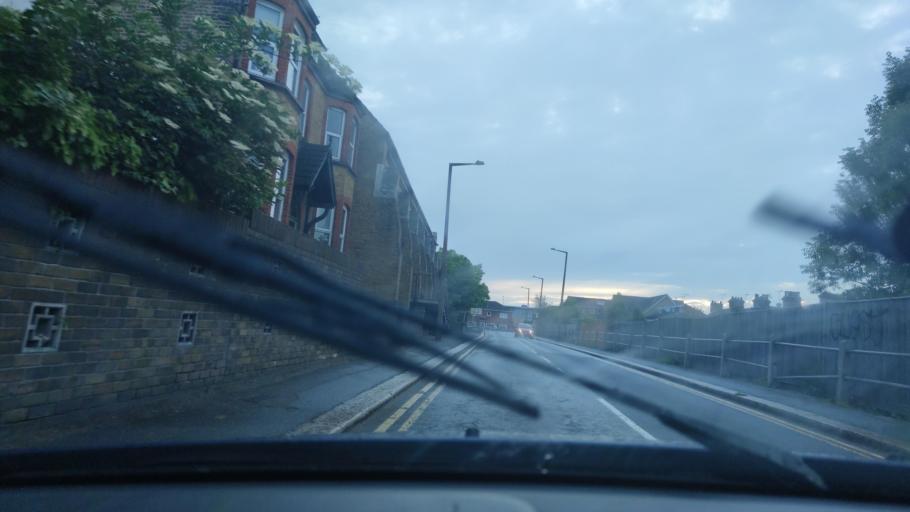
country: GB
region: England
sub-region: Borough of Thurrock
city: Grays
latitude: 51.4766
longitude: 0.3327
